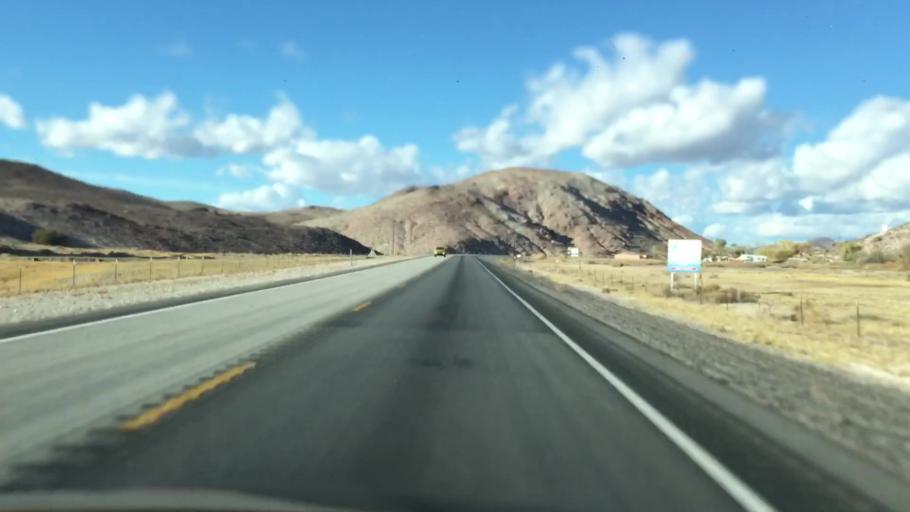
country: US
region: Nevada
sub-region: Nye County
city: Beatty
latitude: 36.9702
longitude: -116.7210
